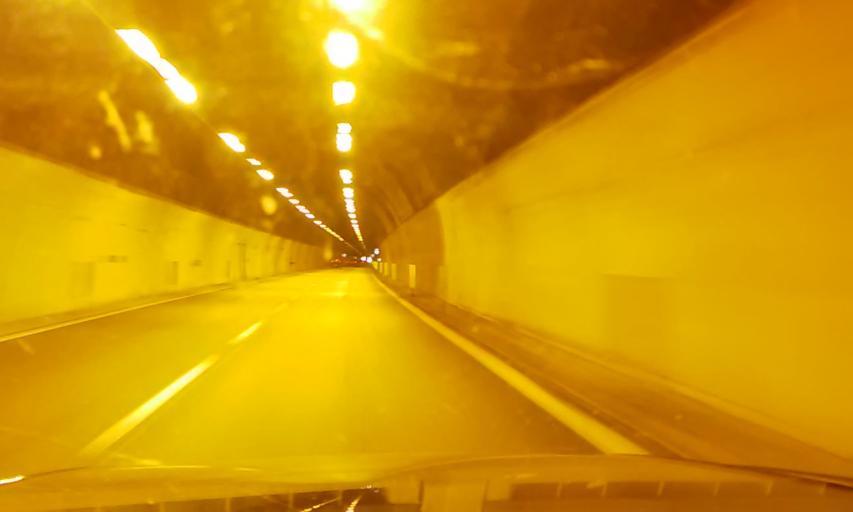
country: IT
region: Liguria
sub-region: Provincia di Savona
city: Borgio
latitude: 44.1781
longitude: 8.2964
